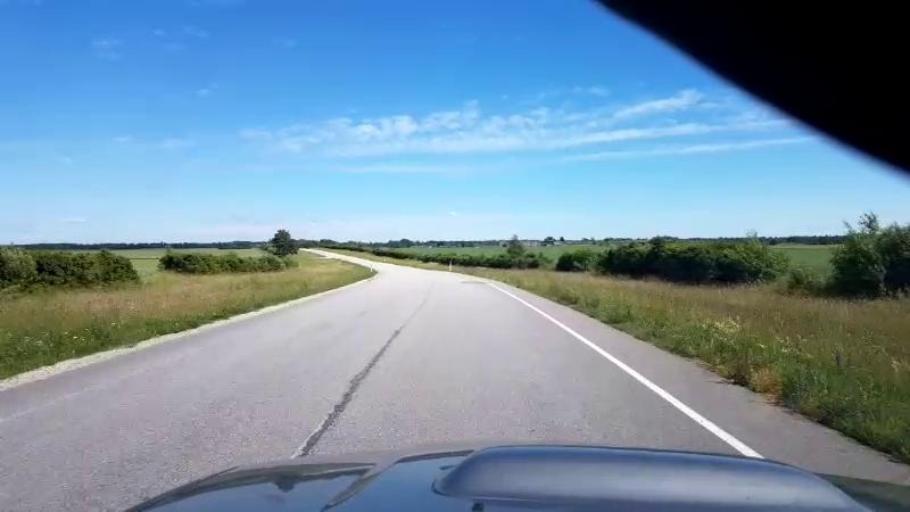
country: EE
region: Jaervamaa
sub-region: Koeru vald
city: Koeru
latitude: 58.9777
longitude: 26.0684
